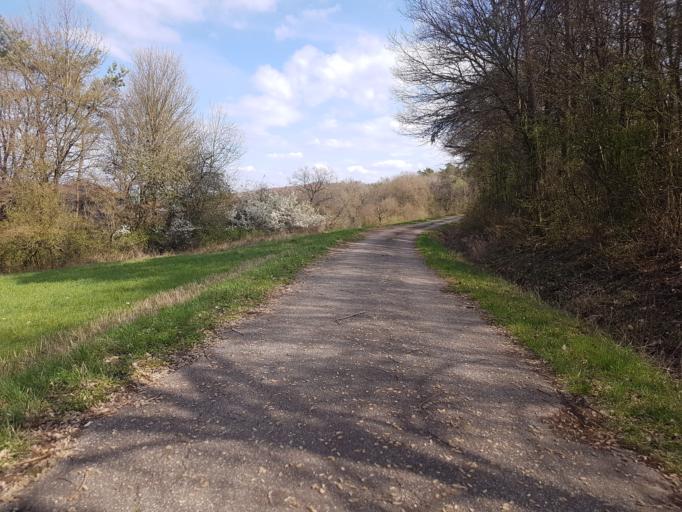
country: DE
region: Baden-Wuerttemberg
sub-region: Regierungsbezirk Stuttgart
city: Niedernhall
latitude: 49.3389
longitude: 9.6209
